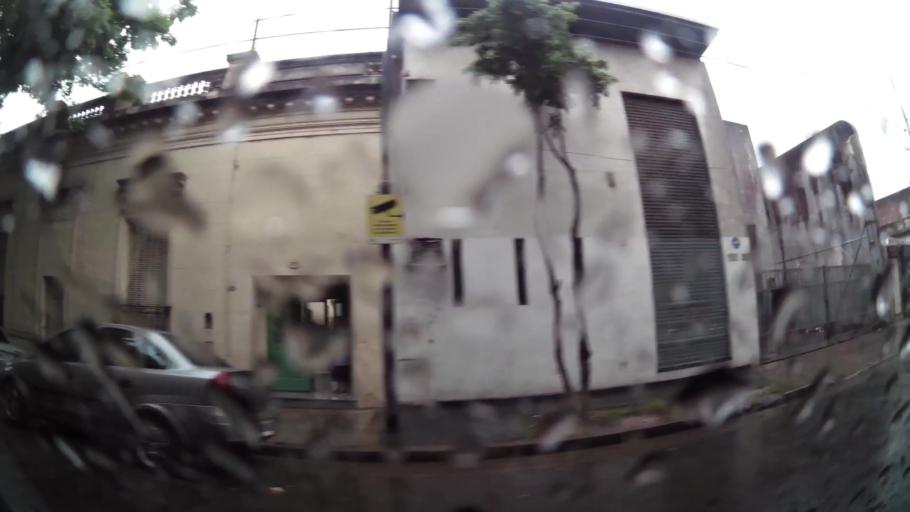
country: AR
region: Buenos Aires F.D.
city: Buenos Aires
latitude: -34.6301
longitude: -58.3842
